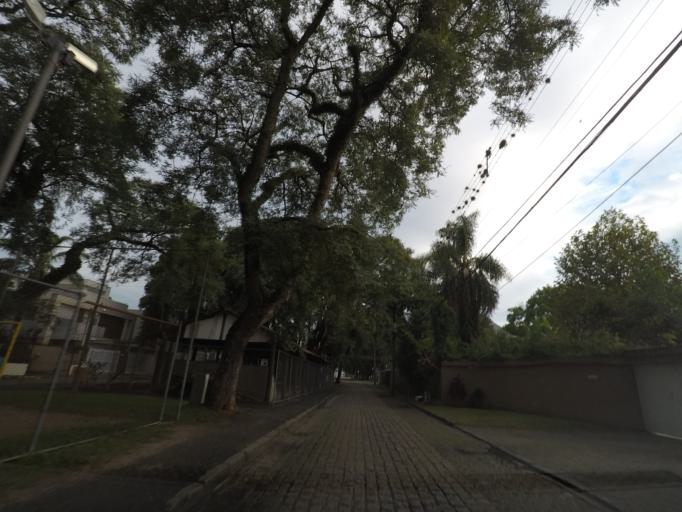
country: BR
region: Parana
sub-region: Curitiba
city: Curitiba
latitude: -25.4250
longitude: -49.2500
